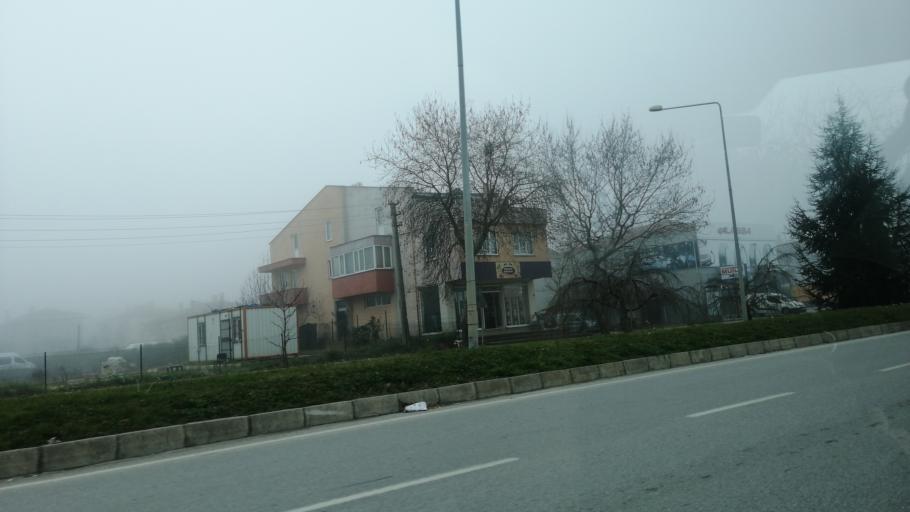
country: TR
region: Yalova
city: Kadikoy
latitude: 40.6509
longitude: 29.2416
